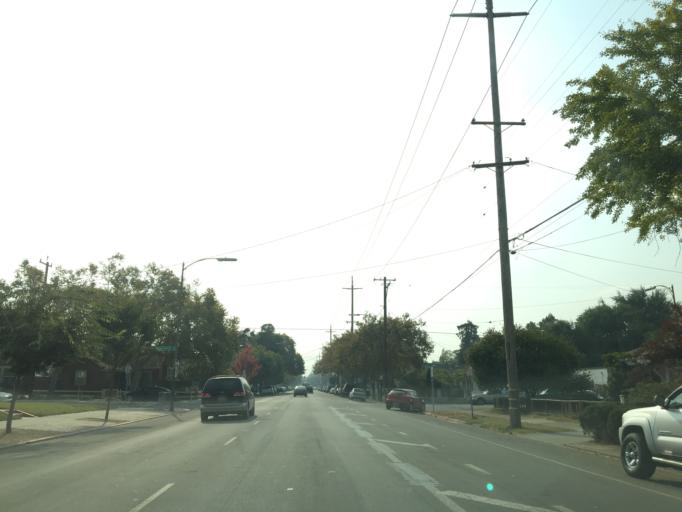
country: US
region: California
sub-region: Santa Clara County
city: San Jose
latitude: 37.3477
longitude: -121.8863
